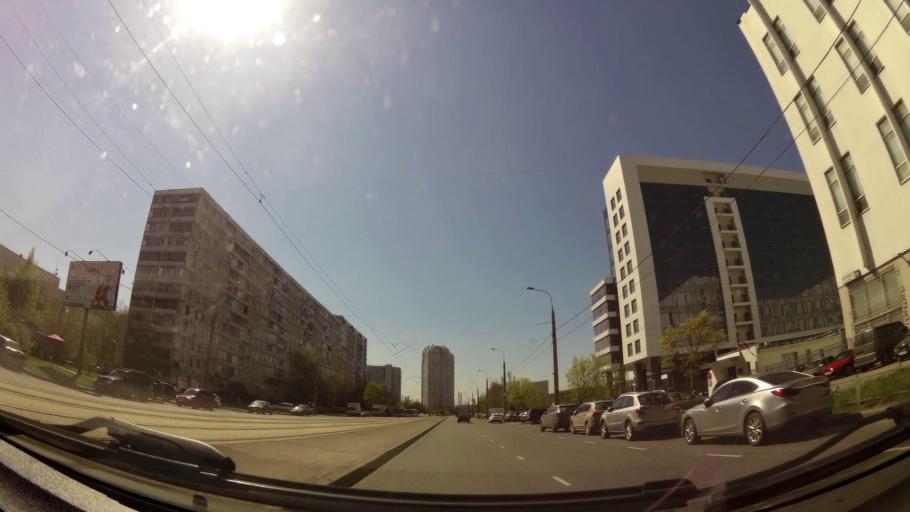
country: RU
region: Moscow
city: Strogino
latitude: 55.8036
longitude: 37.3926
